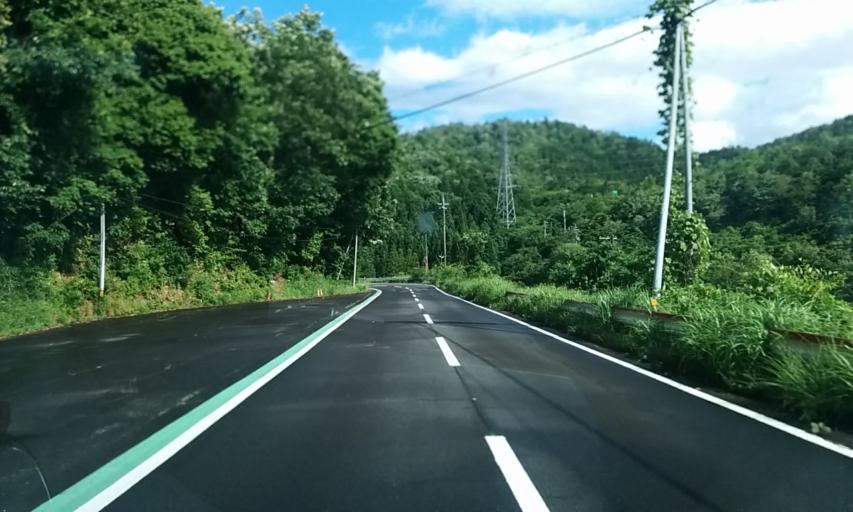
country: JP
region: Kyoto
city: Ayabe
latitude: 35.3834
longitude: 135.2543
